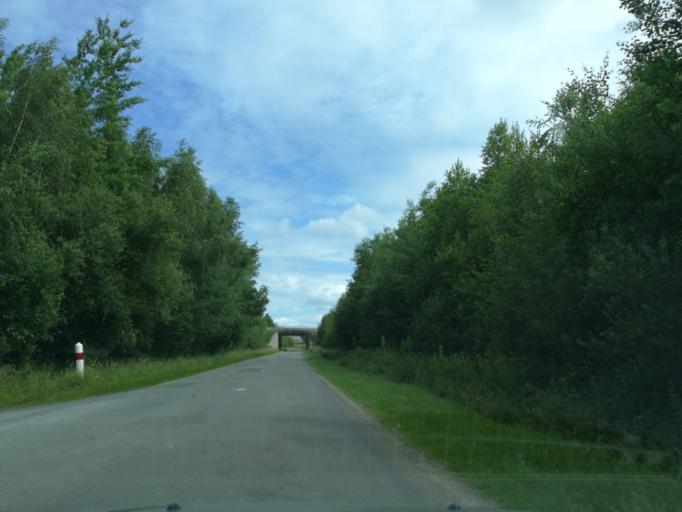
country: FR
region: Brittany
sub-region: Departement d'Ille-et-Vilaine
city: Bedee
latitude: 48.1844
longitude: -1.9849
